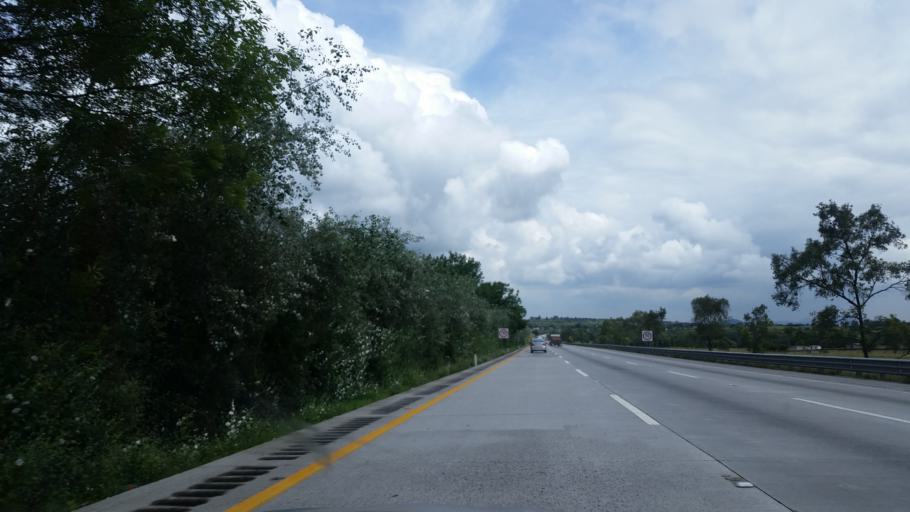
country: MX
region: Mexico
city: San Francisco Soyaniquilpan
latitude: 19.9889
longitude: -99.4564
